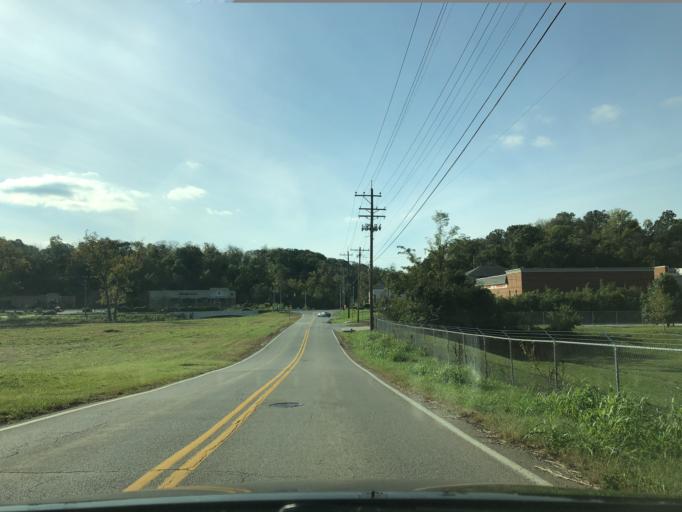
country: US
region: Ohio
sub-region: Hamilton County
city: The Village of Indian Hill
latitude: 39.2504
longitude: -84.2940
